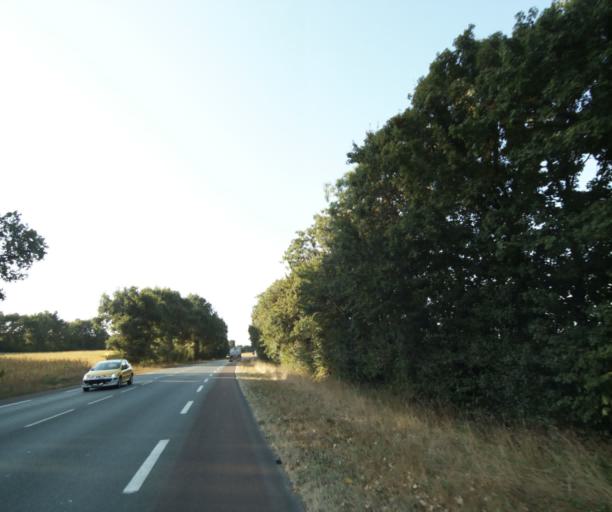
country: FR
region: Poitou-Charentes
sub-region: Departement de la Charente-Maritime
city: Cabariot
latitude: 45.9396
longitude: -0.8641
